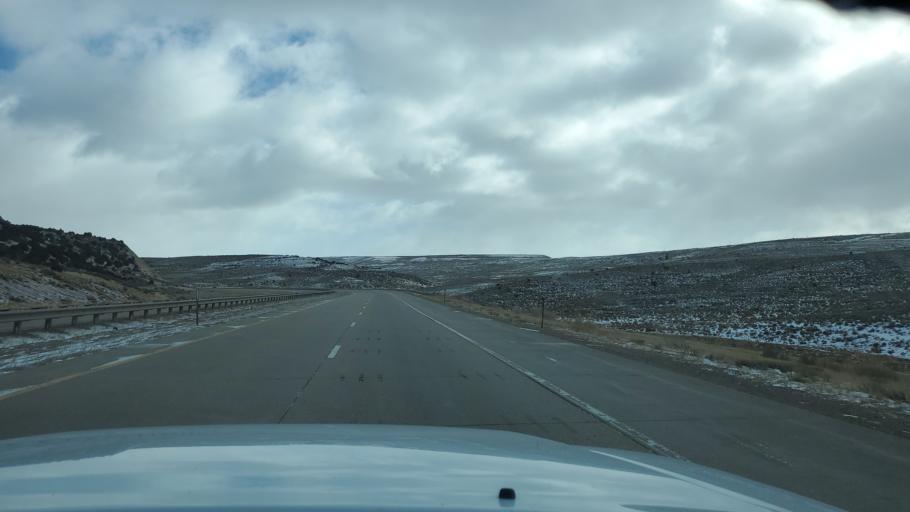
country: US
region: Wyoming
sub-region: Uinta County
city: Evanston
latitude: 41.2698
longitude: -110.8450
